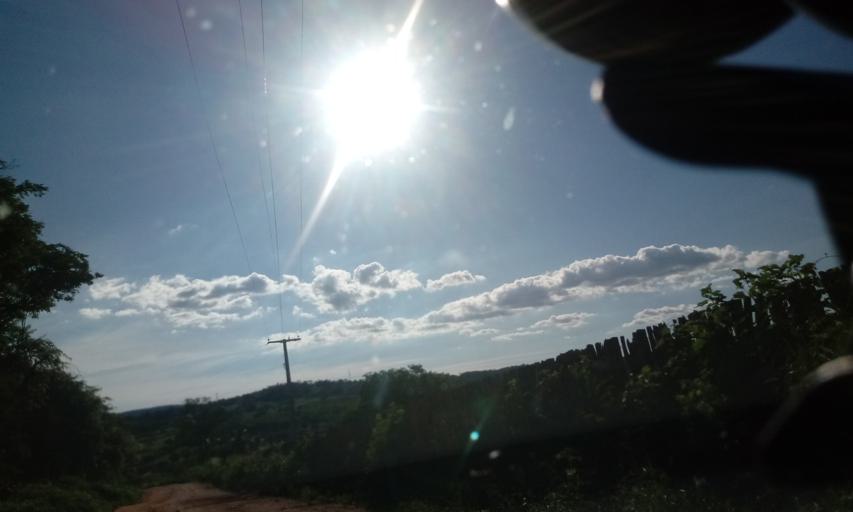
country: BR
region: Bahia
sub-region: Riacho De Santana
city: Riacho de Santana
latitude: -13.8141
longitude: -42.7617
